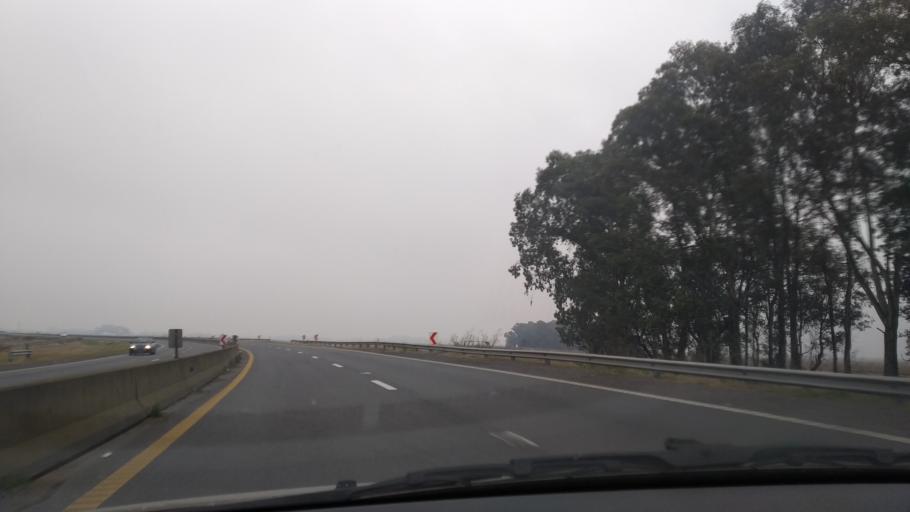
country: AR
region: Buenos Aires
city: Olavarria
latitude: -36.8525
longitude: -60.1101
